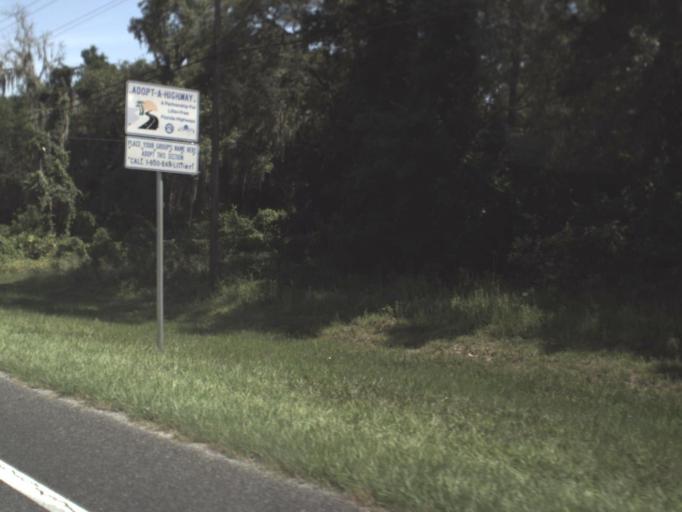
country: US
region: Florida
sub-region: Levy County
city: Manatee Road
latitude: 29.5412
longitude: -82.8942
